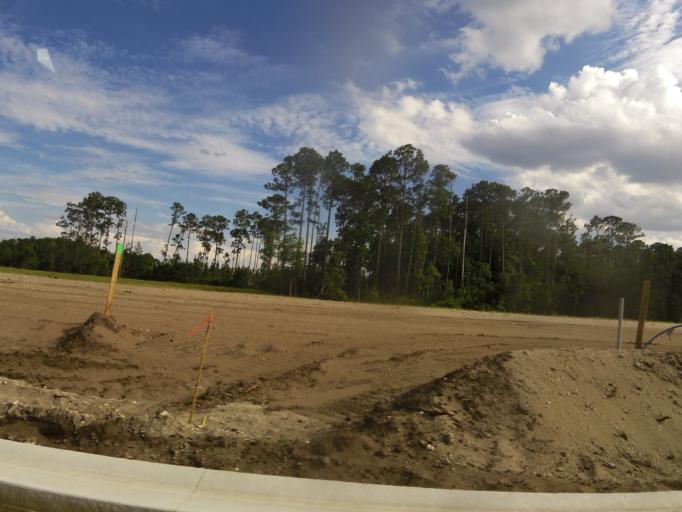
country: US
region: Florida
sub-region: Saint Johns County
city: Palm Valley
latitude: 30.1822
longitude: -81.5099
